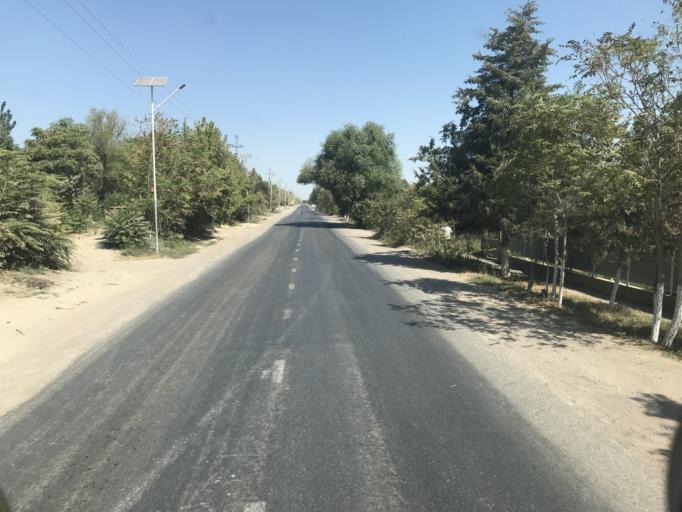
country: KZ
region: Ongtustik Qazaqstan
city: Ilyich
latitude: 40.9352
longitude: 68.4883
